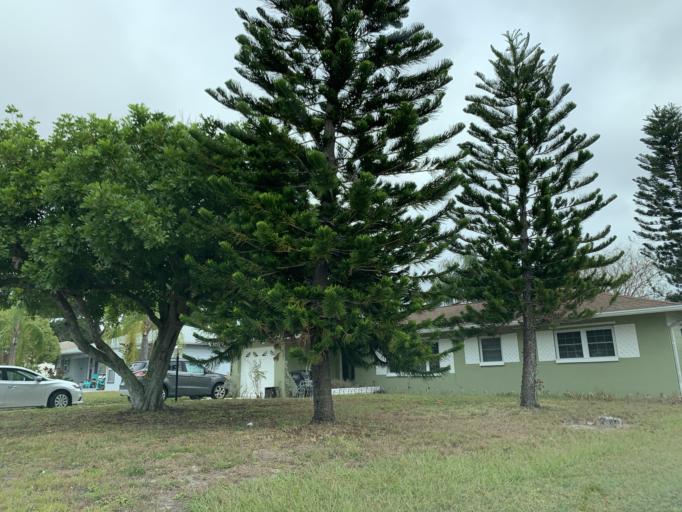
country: US
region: Florida
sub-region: Pinellas County
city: South Highpoint
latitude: 27.9519
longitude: -82.7334
